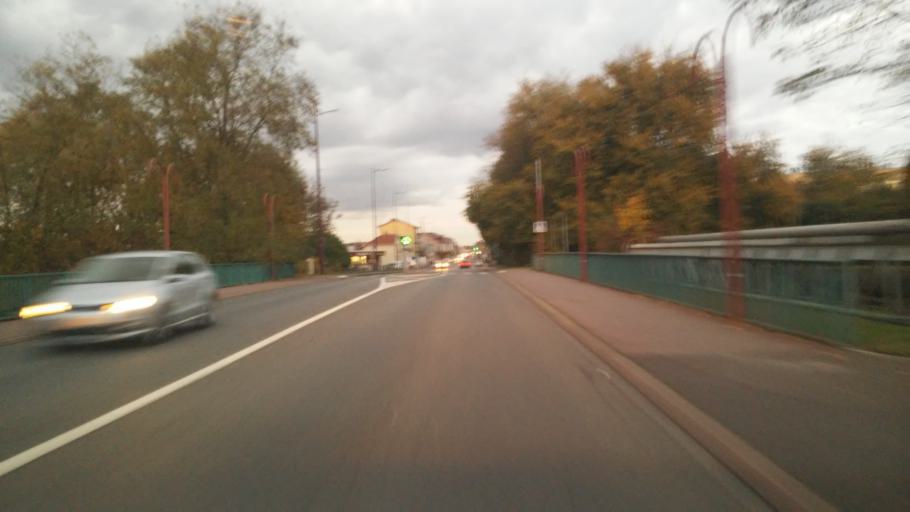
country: FR
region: Lorraine
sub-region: Departement de la Moselle
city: Talange
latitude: 49.2314
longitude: 6.1676
